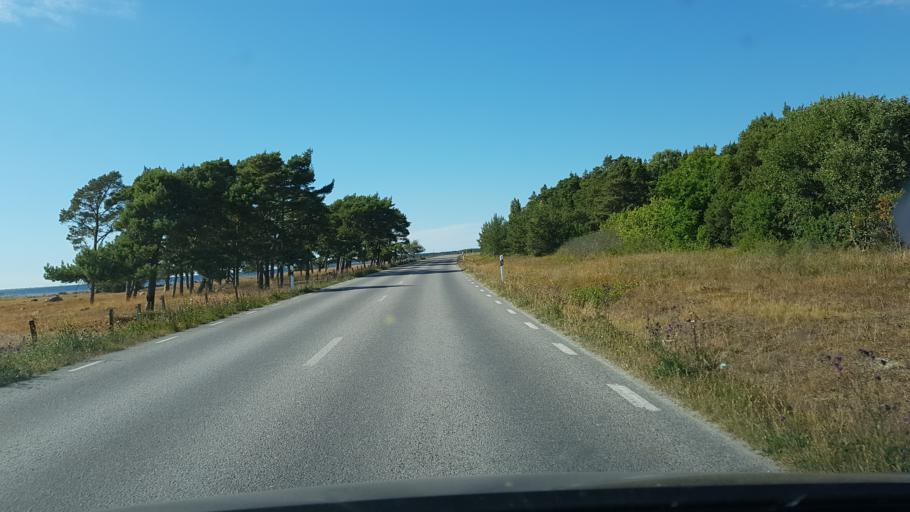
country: SE
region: Gotland
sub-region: Gotland
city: Klintehamn
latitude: 57.4168
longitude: 18.1527
